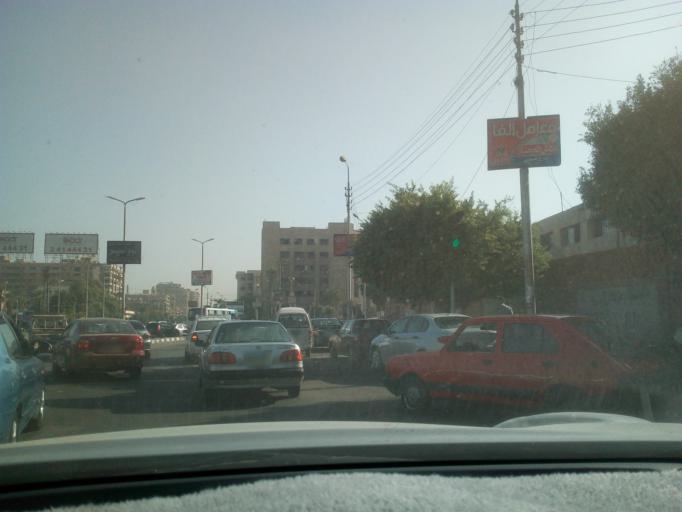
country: EG
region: Muhafazat al Qahirah
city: Cairo
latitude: 30.1031
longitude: 31.3279
